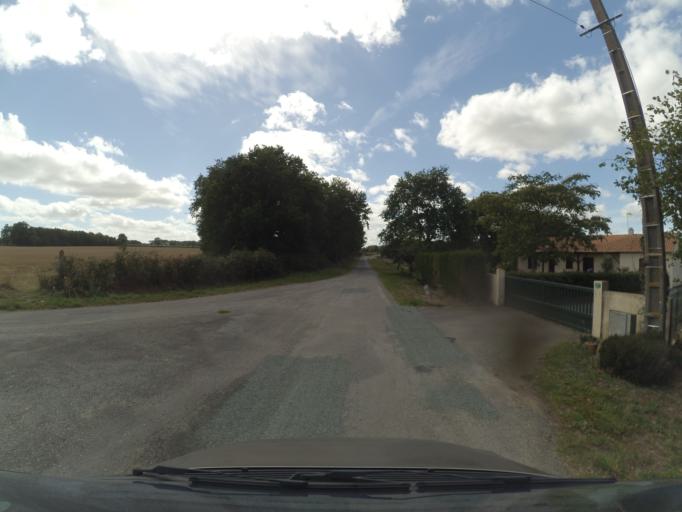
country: FR
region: Pays de la Loire
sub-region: Departement de la Loire-Atlantique
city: Remouille
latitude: 47.0459
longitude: -1.4003
